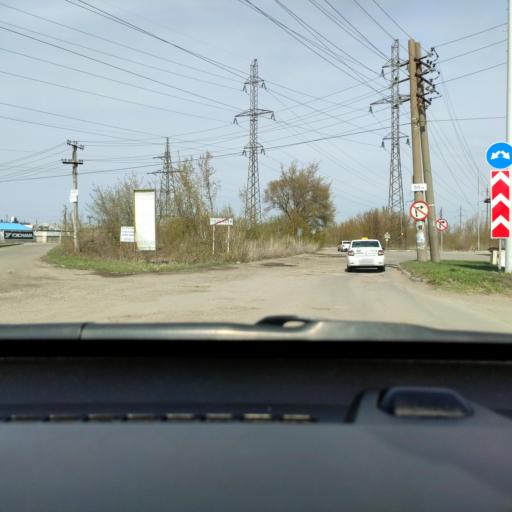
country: RU
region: Samara
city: Tol'yatti
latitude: 53.5792
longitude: 49.2933
